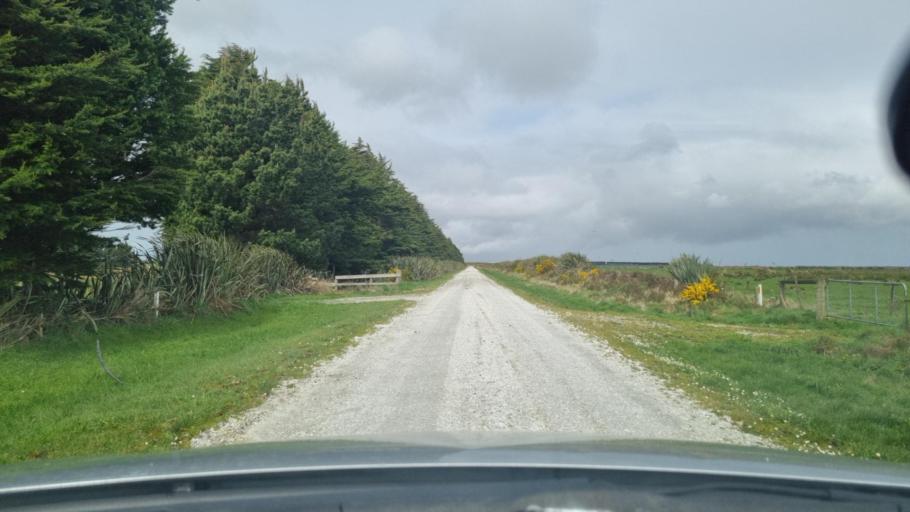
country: NZ
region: Southland
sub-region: Invercargill City
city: Bluff
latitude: -46.5145
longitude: 168.3573
